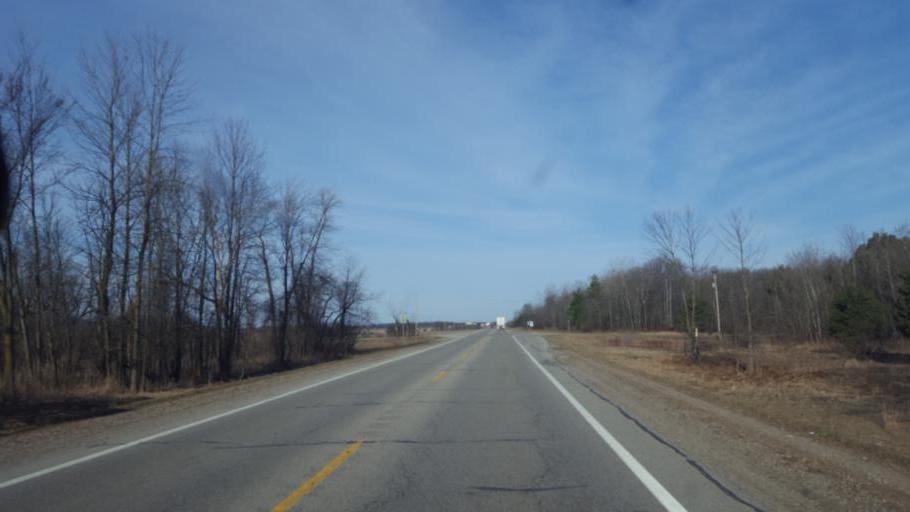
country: US
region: Michigan
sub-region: Montcalm County
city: Lakeview
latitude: 43.4301
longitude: -85.1818
